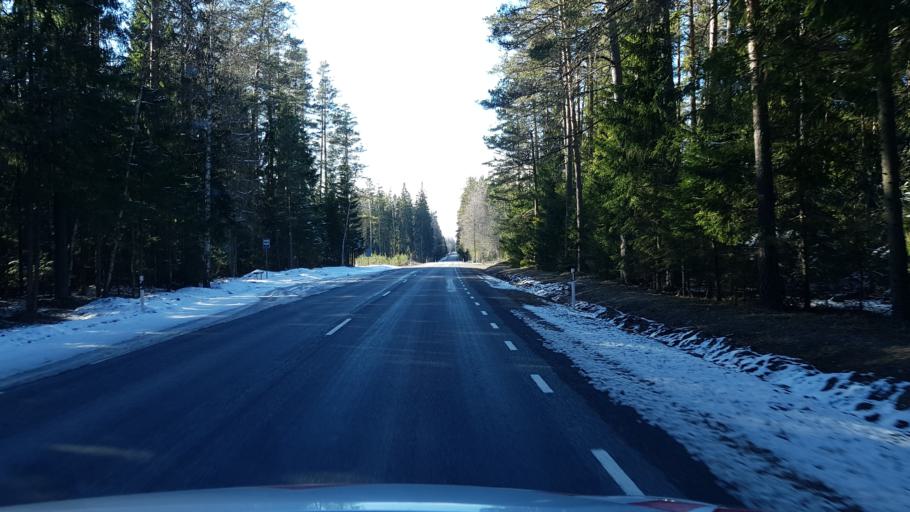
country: EE
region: Laeaene-Virumaa
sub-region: Tapa vald
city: Tapa
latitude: 59.4281
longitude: 25.9781
